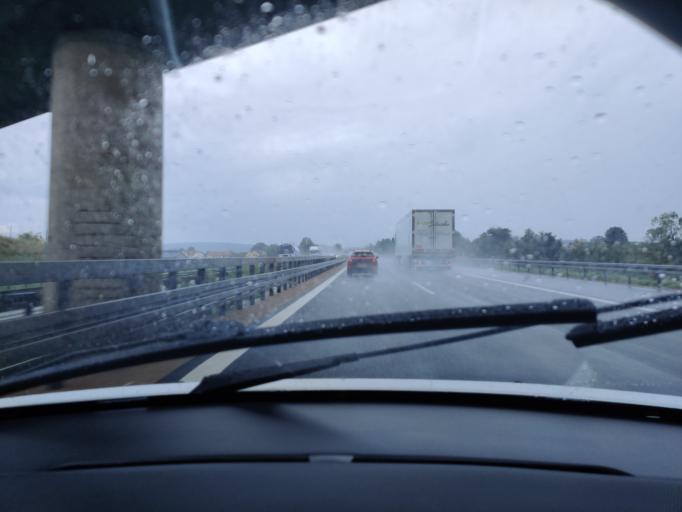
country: DE
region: Bavaria
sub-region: Upper Palatinate
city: Stulln
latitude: 49.4163
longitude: 12.1661
